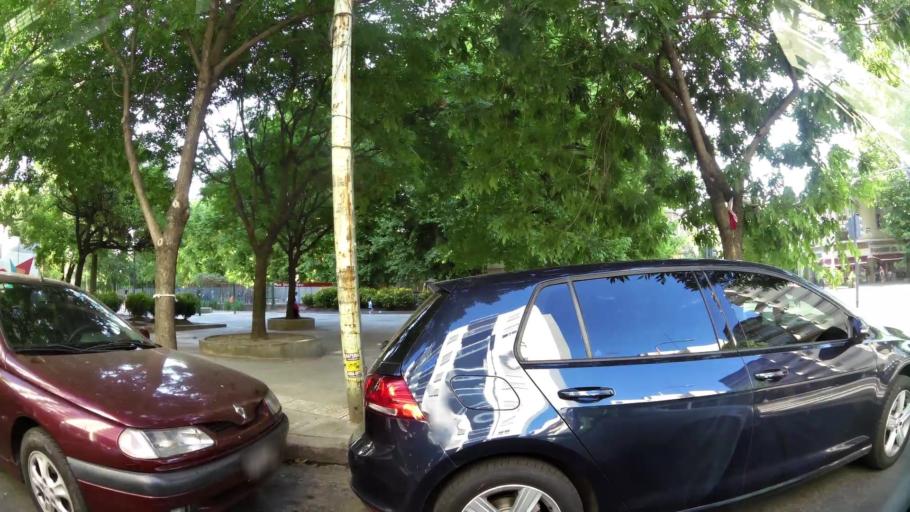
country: AR
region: Buenos Aires F.D.
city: Villa Santa Rita
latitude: -34.6163
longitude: -58.4404
